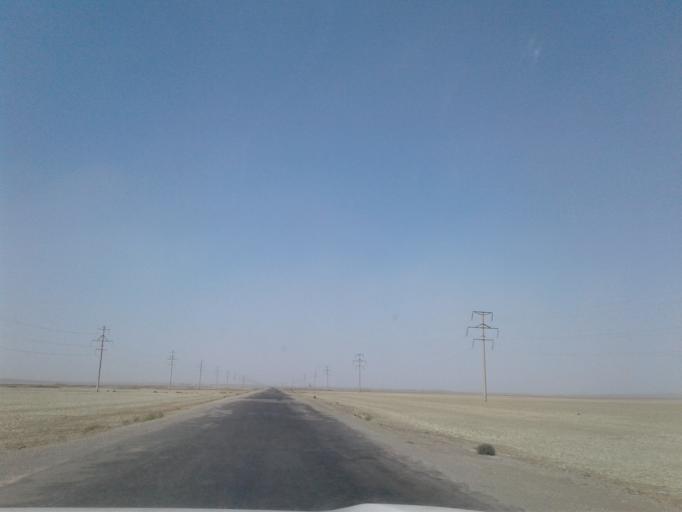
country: TM
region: Balkan
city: Gumdag
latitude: 39.0690
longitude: 54.5845
